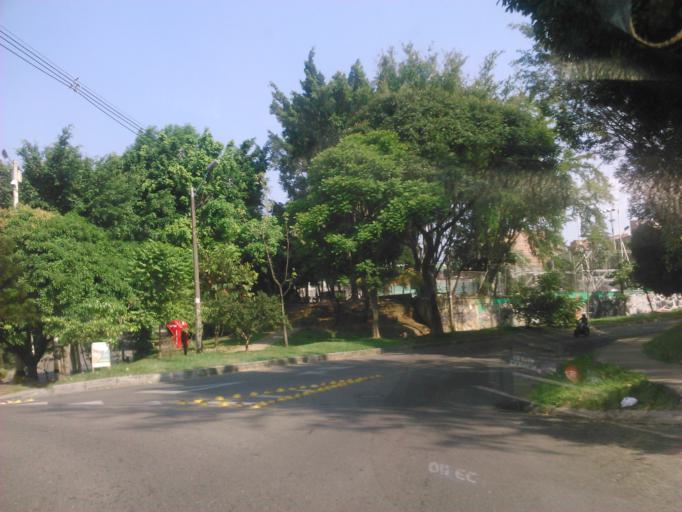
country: CO
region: Antioquia
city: Medellin
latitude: 6.2514
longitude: -75.6143
